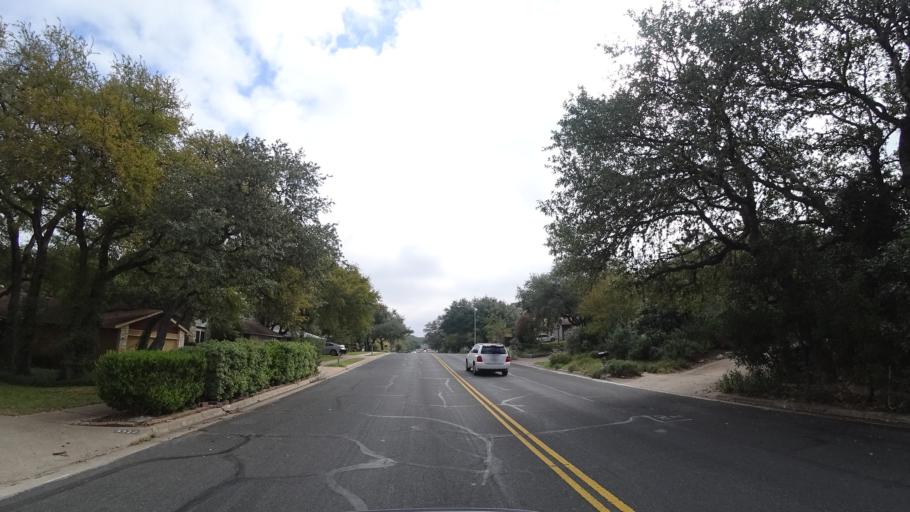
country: US
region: Texas
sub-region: Travis County
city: Shady Hollow
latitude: 30.2058
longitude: -97.8324
